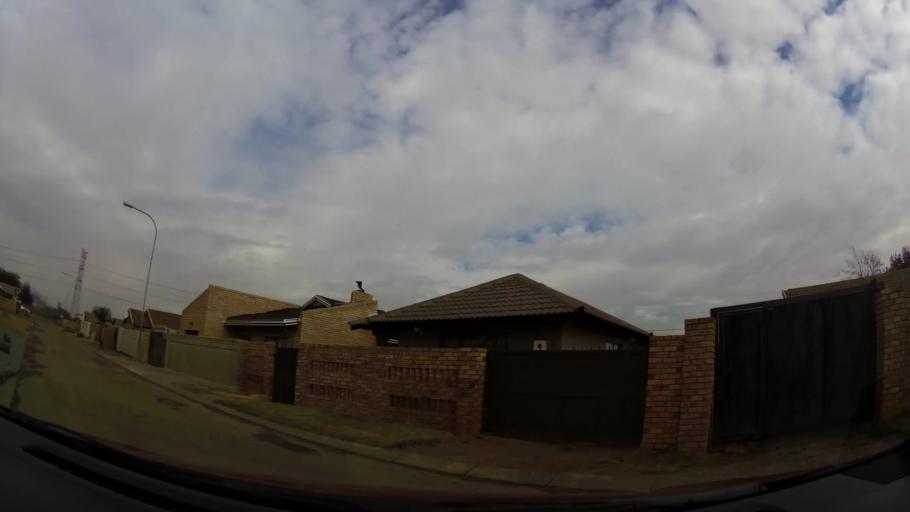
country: ZA
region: Gauteng
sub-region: City of Johannesburg Metropolitan Municipality
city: Soweto
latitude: -26.2711
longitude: 27.8396
